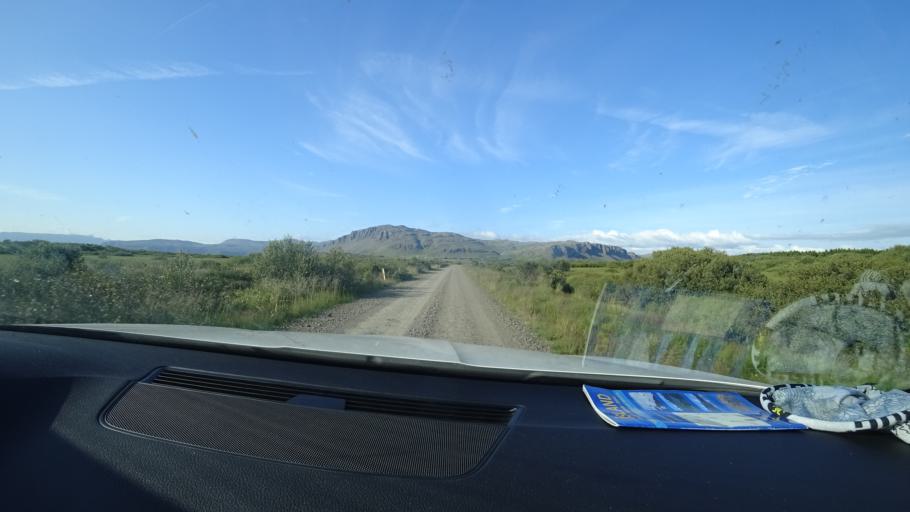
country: IS
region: West
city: Borgarnes
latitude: 64.6777
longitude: -21.9556
